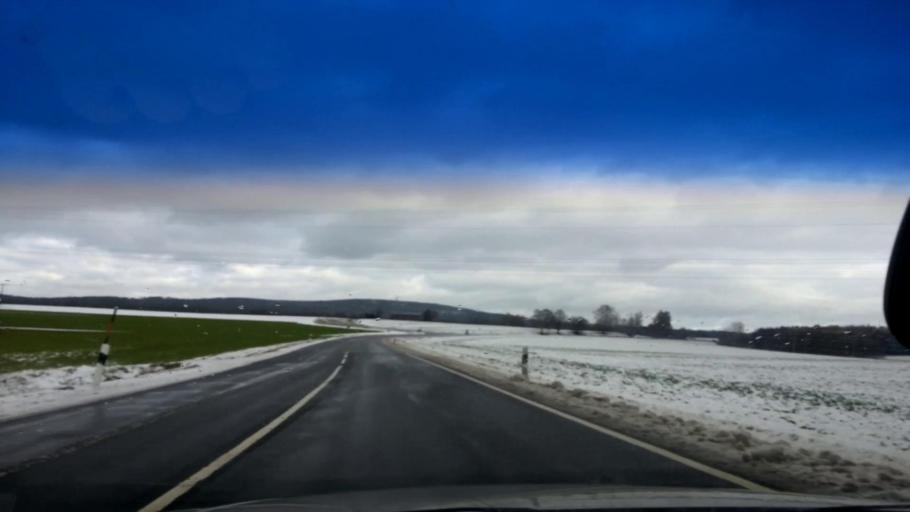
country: DE
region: Bavaria
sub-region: Upper Franconia
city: Marktleuthen
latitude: 50.1376
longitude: 12.0124
